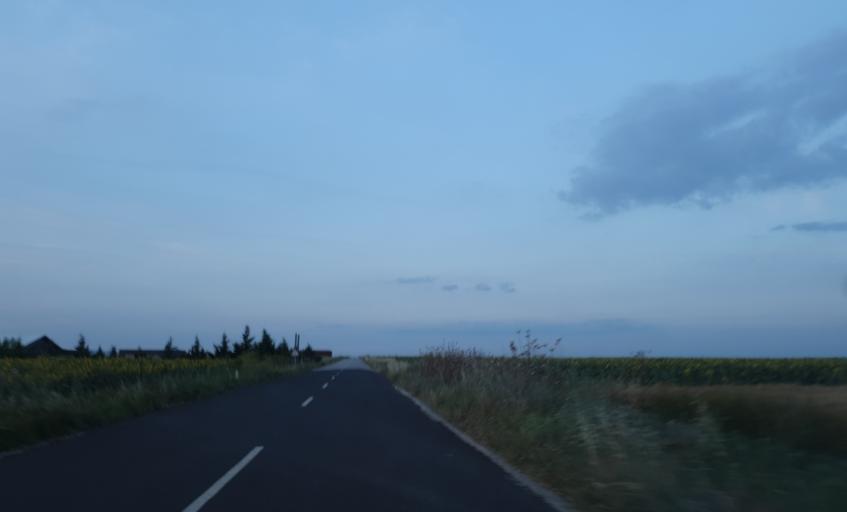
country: TR
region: Tekirdag
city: Beyazkoy
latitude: 41.4183
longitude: 27.6648
